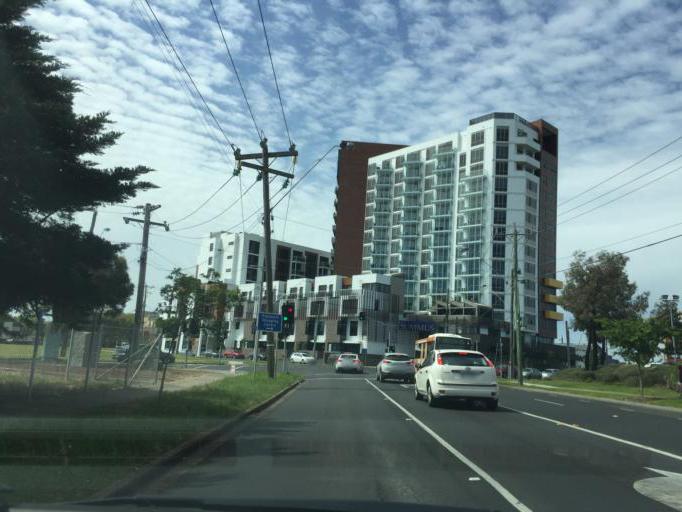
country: AU
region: Victoria
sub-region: Maribyrnong
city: Maribyrnong
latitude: -37.7754
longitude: 144.8805
